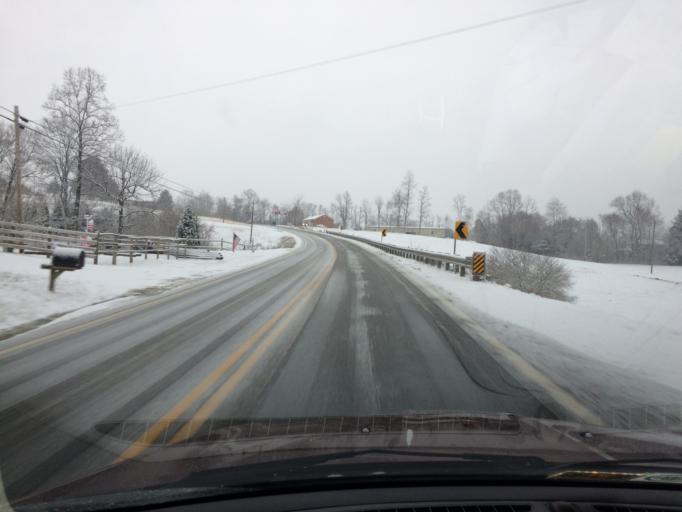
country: US
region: Virginia
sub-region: Amherst County
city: Amherst
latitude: 37.6243
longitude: -79.1147
